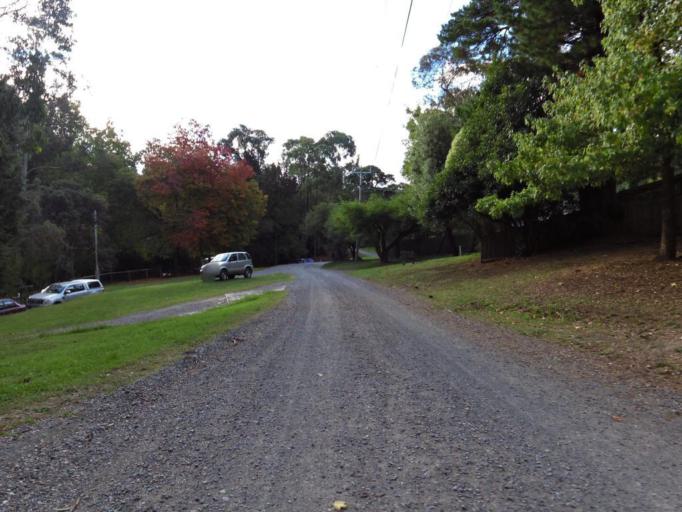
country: AU
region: Victoria
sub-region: Yarra Ranges
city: Mount Evelyn
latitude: -37.7925
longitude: 145.3852
